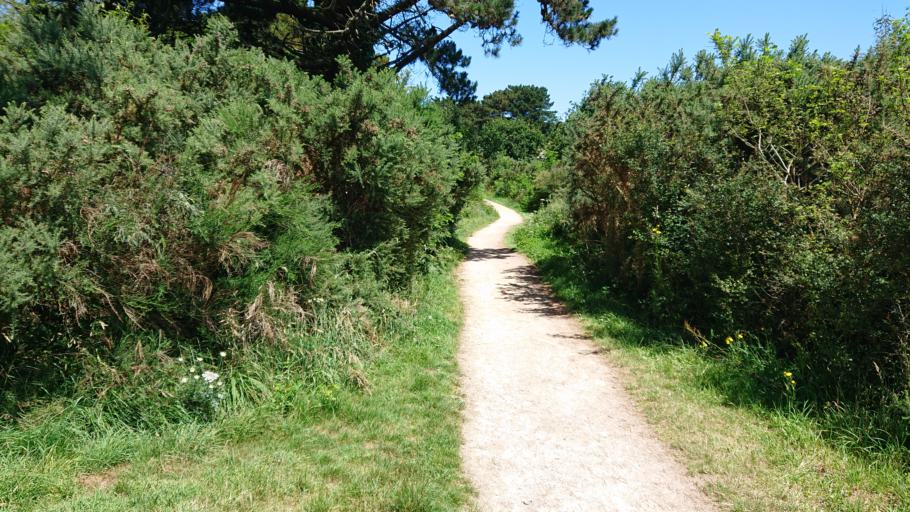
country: FR
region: Brittany
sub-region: Departement des Cotes-d'Armor
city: Tregastel
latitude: 48.8287
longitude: -3.4791
